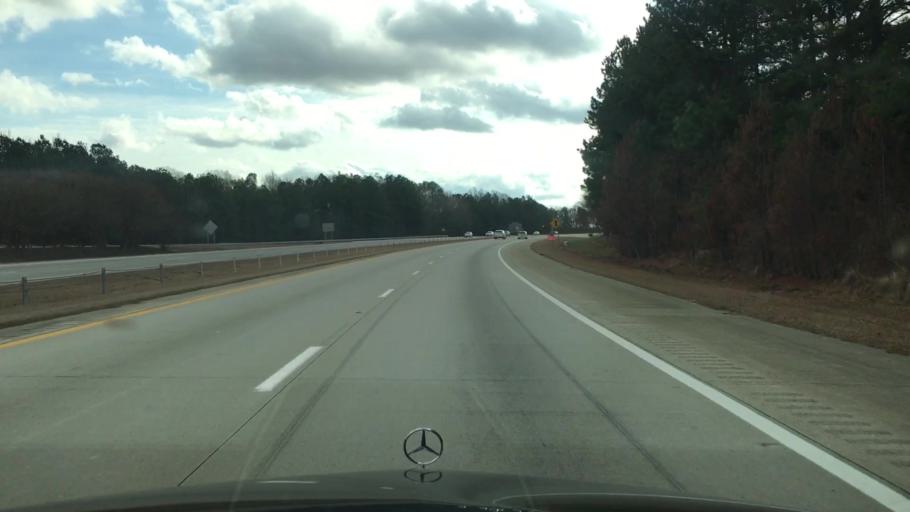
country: US
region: North Carolina
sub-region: Johnston County
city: Clayton
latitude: 35.6056
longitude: -78.5638
